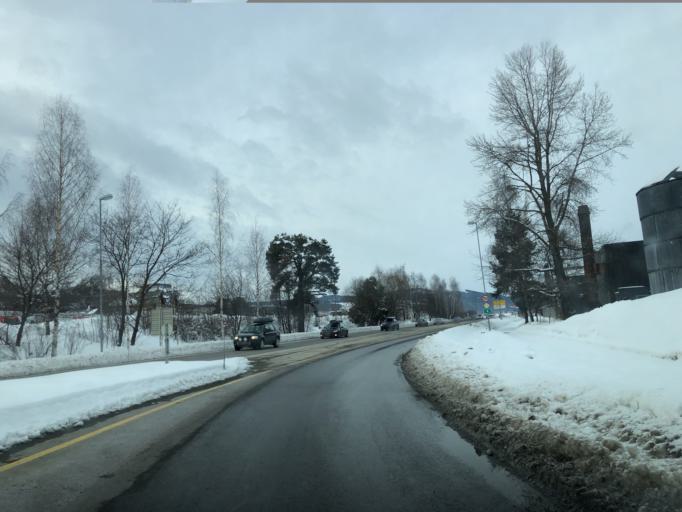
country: NO
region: Oppland
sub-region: Gjovik
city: Gjovik
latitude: 60.7956
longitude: 10.6967
